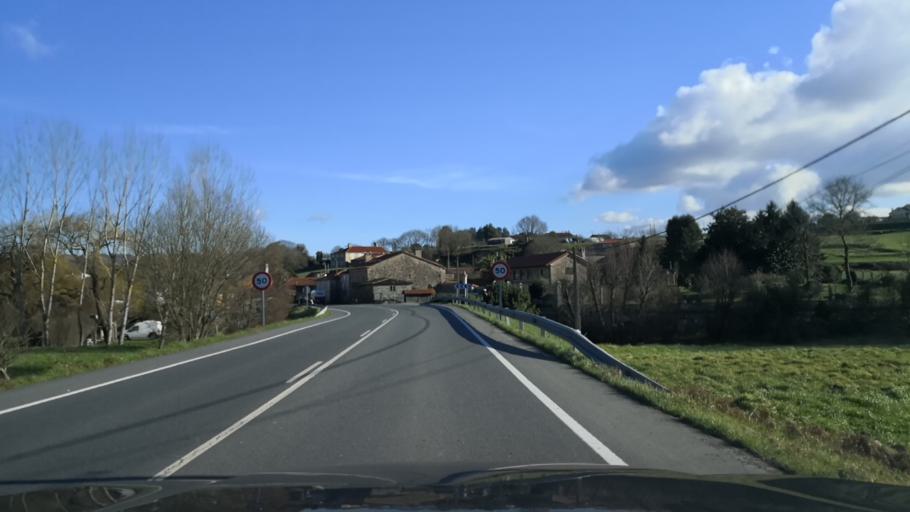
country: ES
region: Galicia
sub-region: Provincia de Pontevedra
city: Silleda
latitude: 42.7243
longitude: -8.2966
